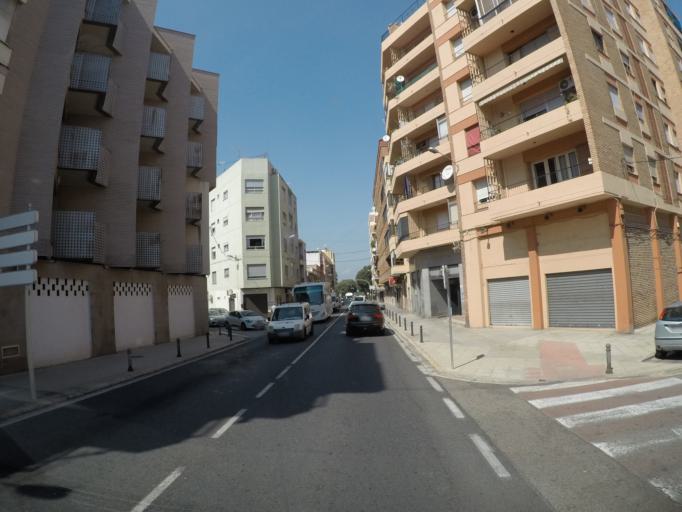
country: ES
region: Valencia
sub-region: Provincia de Valencia
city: Oliva
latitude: 38.9218
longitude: -0.1228
